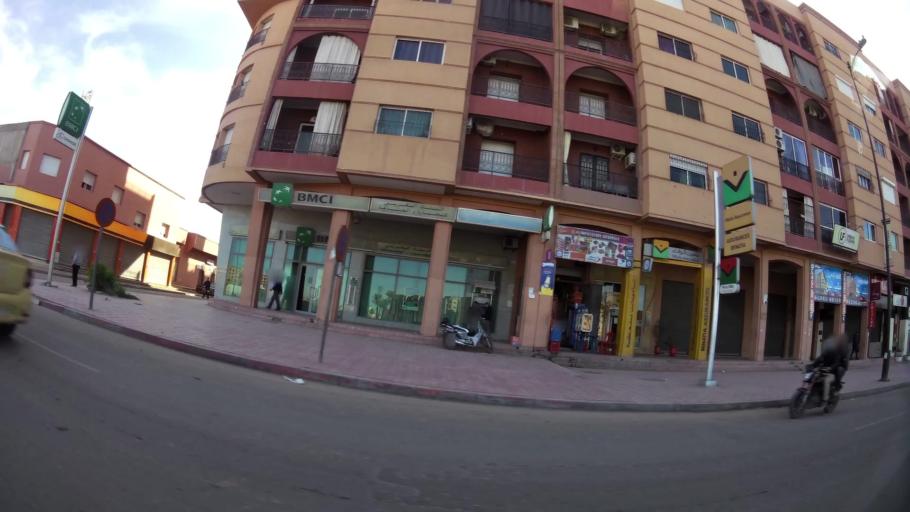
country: MA
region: Marrakech-Tensift-Al Haouz
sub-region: Marrakech
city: Marrakesh
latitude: 31.6569
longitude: -8.0220
